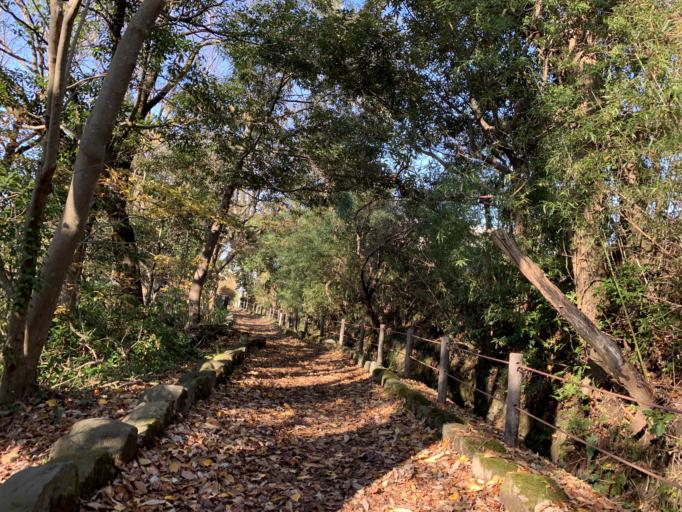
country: JP
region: Ishikawa
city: Nonoichi
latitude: 36.5399
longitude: 136.6859
